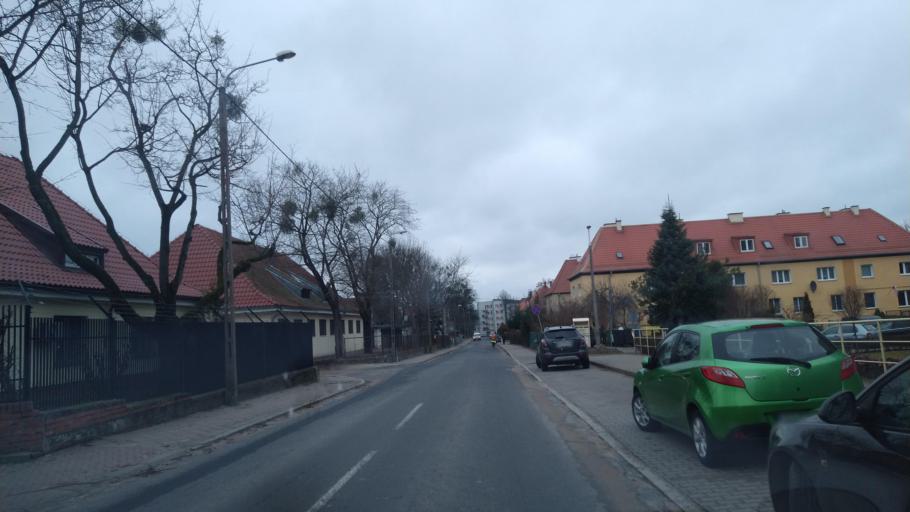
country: PL
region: Warmian-Masurian Voivodeship
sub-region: Powiat olsztynski
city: Olsztyn
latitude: 53.7928
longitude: 20.4946
